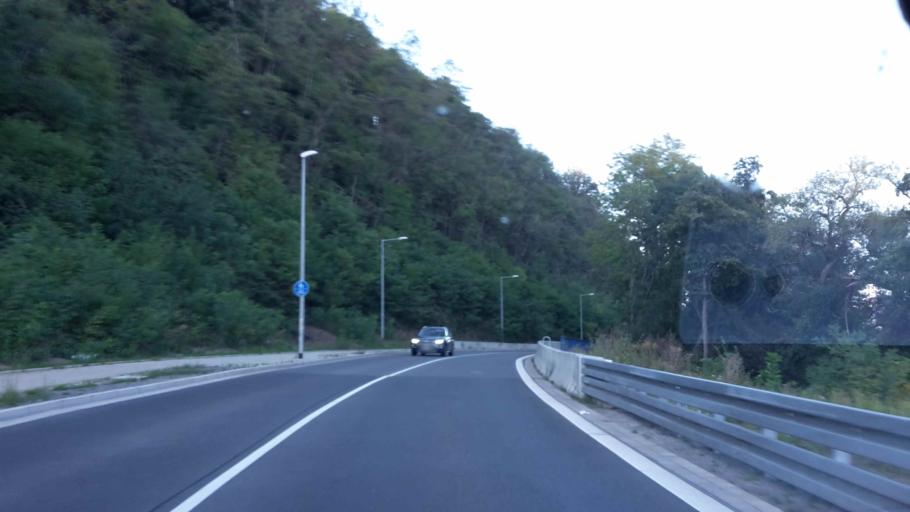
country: DE
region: North Rhine-Westphalia
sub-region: Regierungsbezirk Arnsberg
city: Hagen
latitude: 51.3595
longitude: 7.4549
